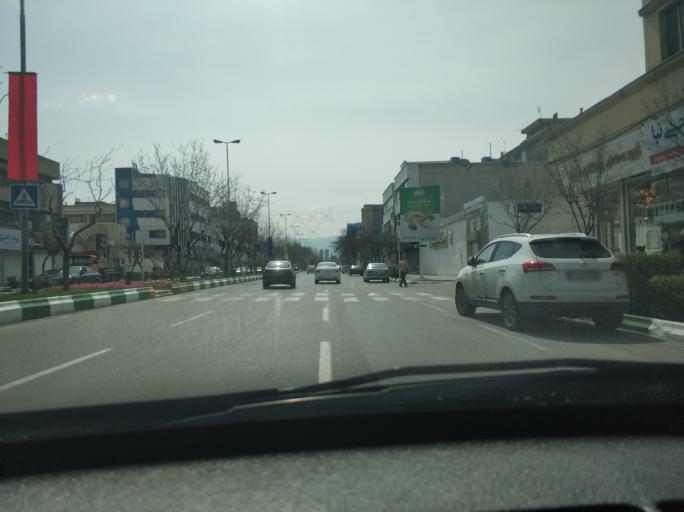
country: IR
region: Razavi Khorasan
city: Mashhad
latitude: 36.3034
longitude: 59.5649
